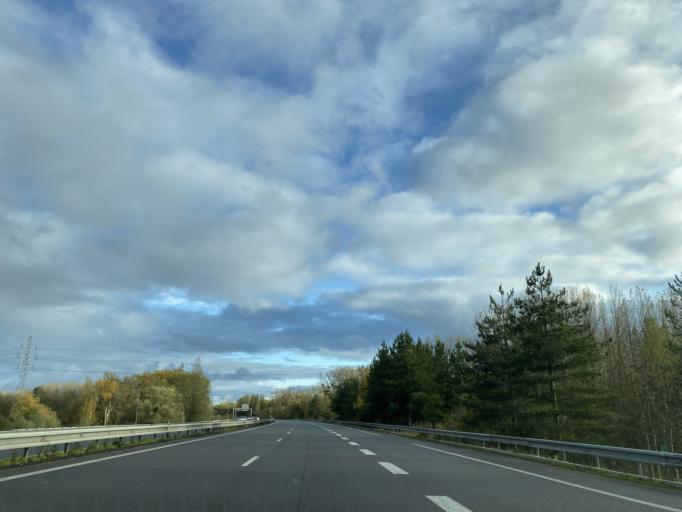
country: FR
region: Centre
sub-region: Departement du Cher
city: Vierzon
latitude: 47.2077
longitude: 2.1199
